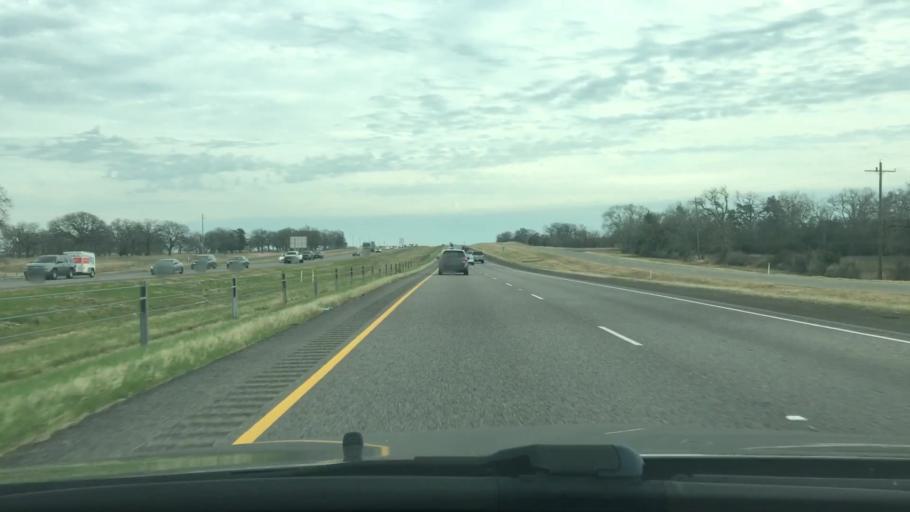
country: US
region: Texas
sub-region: Madison County
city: Madisonville
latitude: 30.9545
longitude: -95.8687
